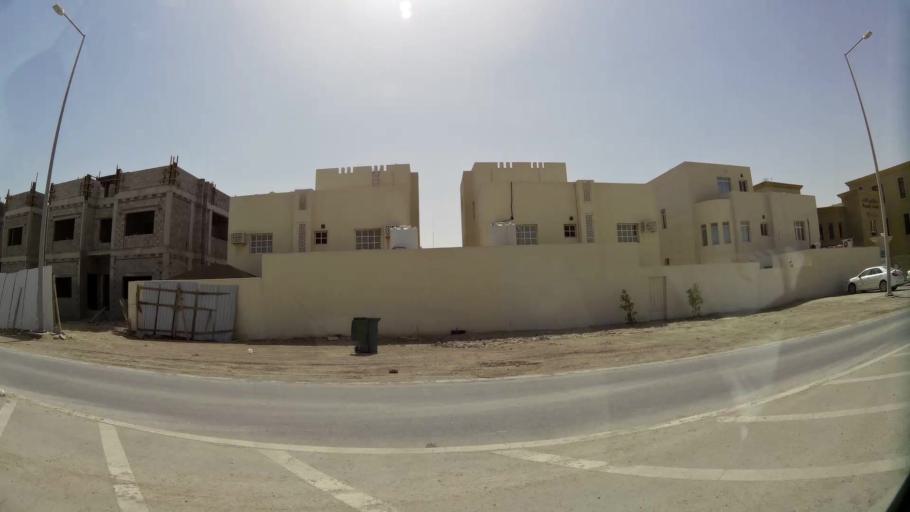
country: QA
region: Baladiyat Umm Salal
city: Umm Salal Muhammad
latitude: 25.3710
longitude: 51.4418
